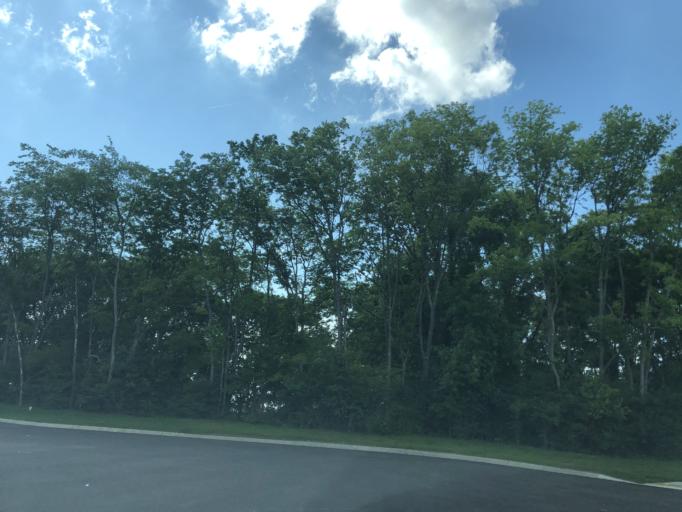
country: US
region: Tennessee
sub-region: Davidson County
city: Nashville
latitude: 36.2373
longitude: -86.8160
